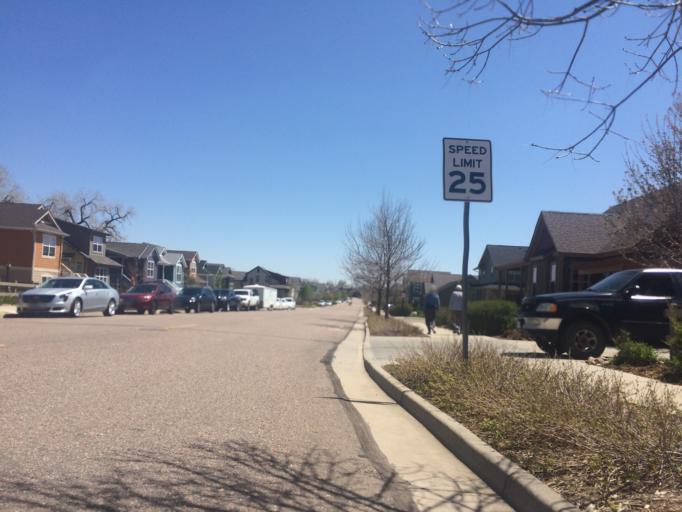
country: US
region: Colorado
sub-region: Boulder County
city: Louisville
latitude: 39.9985
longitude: -105.1338
